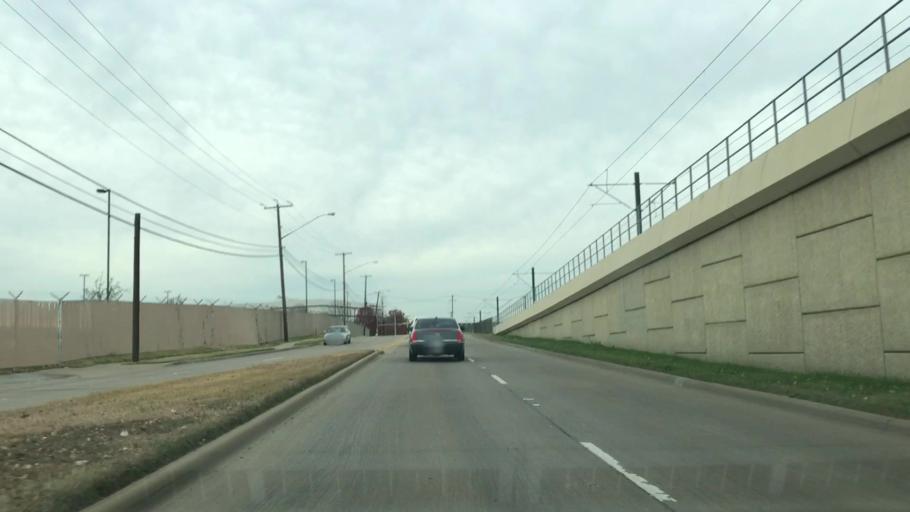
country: US
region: Texas
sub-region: Dallas County
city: University Park
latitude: 32.8454
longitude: -96.8681
